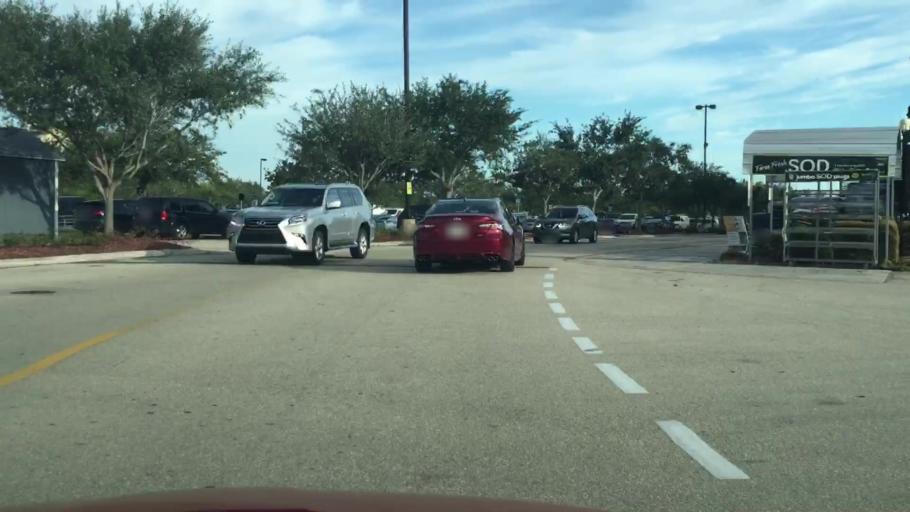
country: US
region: Florida
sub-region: Lee County
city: Villas
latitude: 26.5286
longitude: -81.8681
